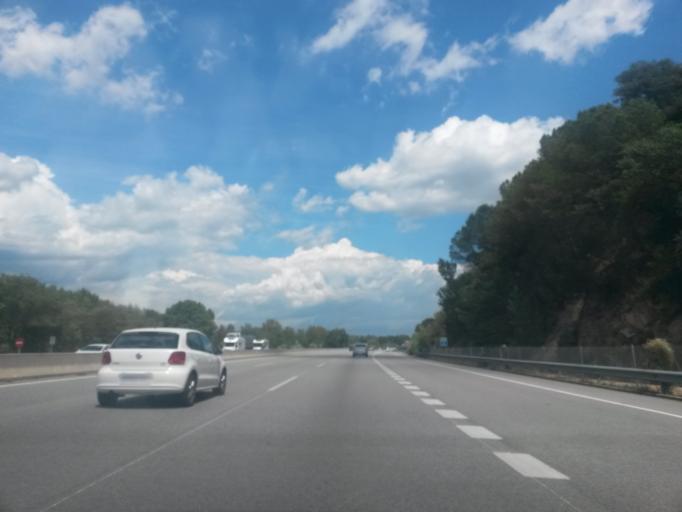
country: ES
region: Catalonia
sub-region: Provincia de Barcelona
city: Sant Celoni
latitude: 41.7015
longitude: 2.5186
